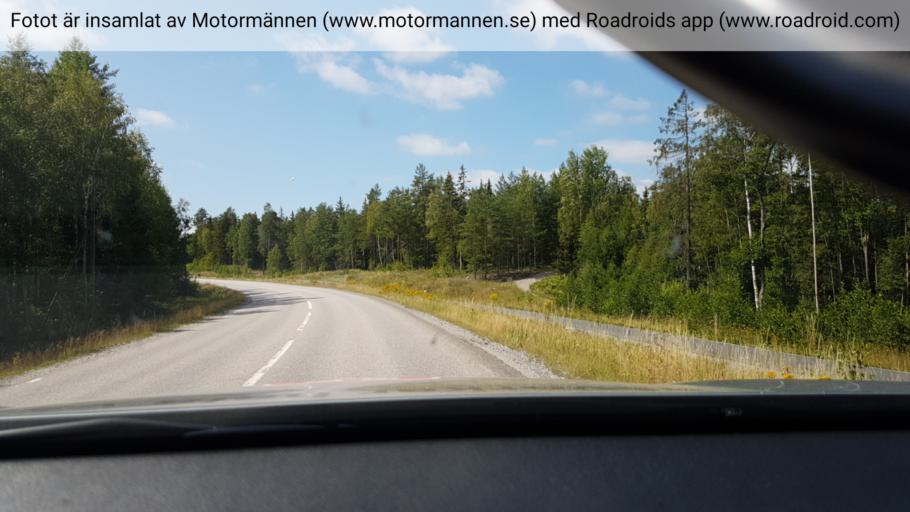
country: SE
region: Stockholm
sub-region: Vallentuna Kommun
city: Vallentuna
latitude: 59.5333
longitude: 18.1181
